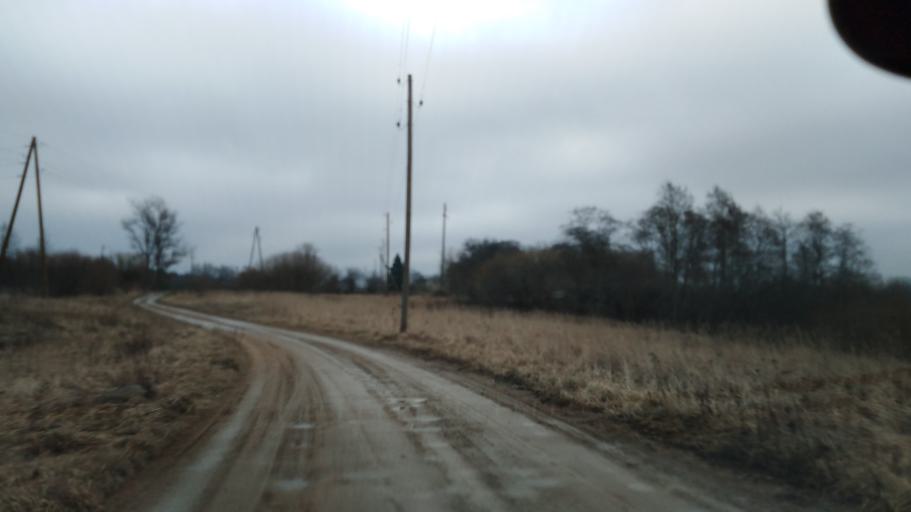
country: LV
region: Kuldigas Rajons
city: Kuldiga
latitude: 56.9839
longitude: 21.9678
